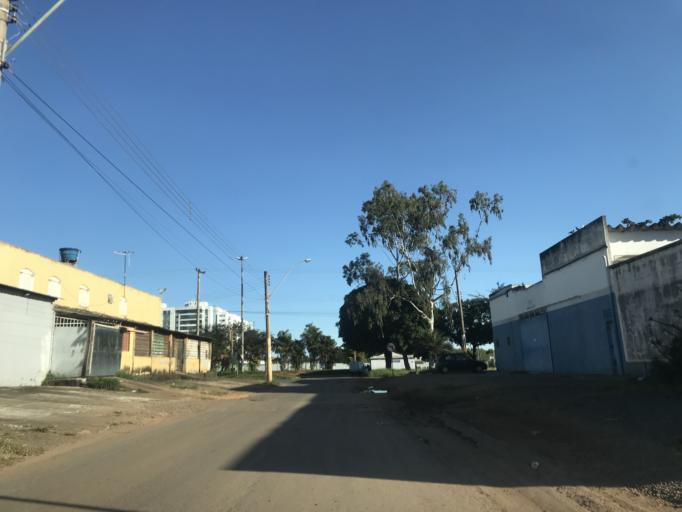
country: BR
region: Federal District
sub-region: Brasilia
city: Brasilia
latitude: -15.8264
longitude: -47.9588
